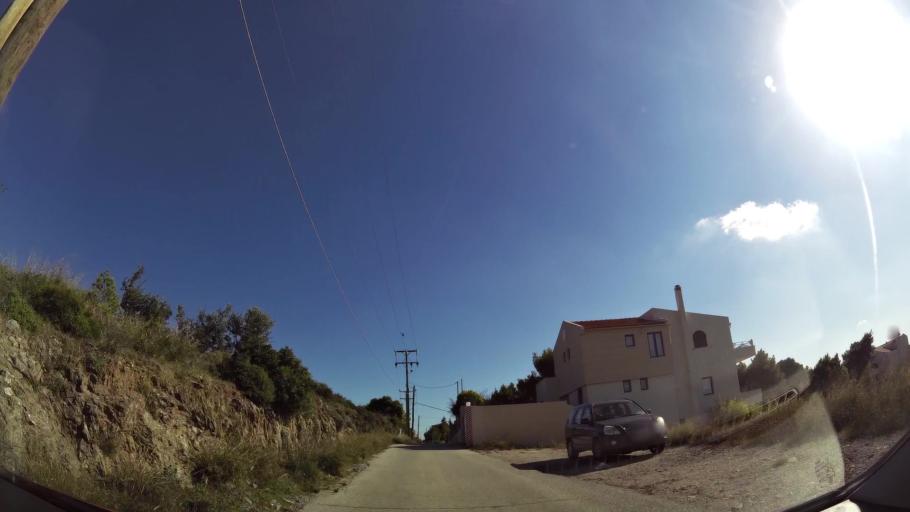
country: GR
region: Attica
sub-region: Nomarchia Anatolikis Attikis
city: Dioni
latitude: 38.0383
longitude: 23.9312
